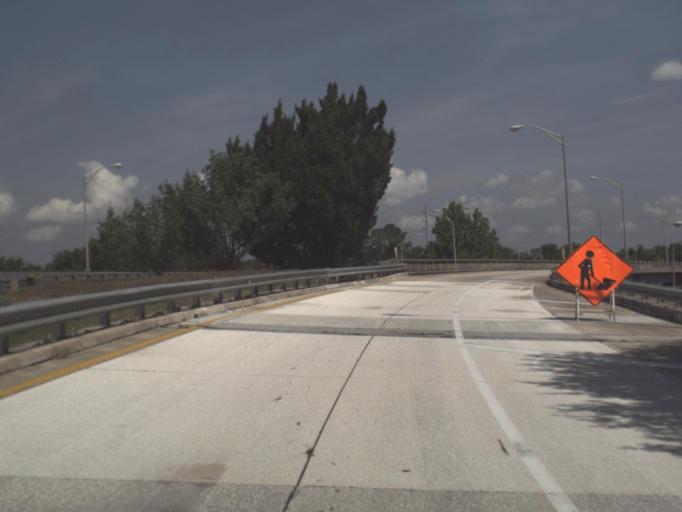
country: US
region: Florida
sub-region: Duval County
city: Jacksonville
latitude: 30.3302
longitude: -81.6359
